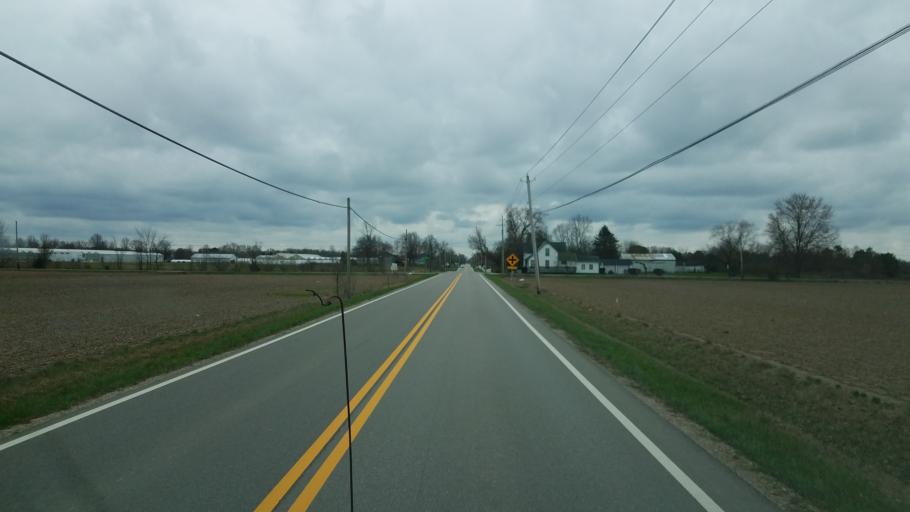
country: US
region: Ohio
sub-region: Delaware County
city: Delaware
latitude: 40.2381
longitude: -83.1315
